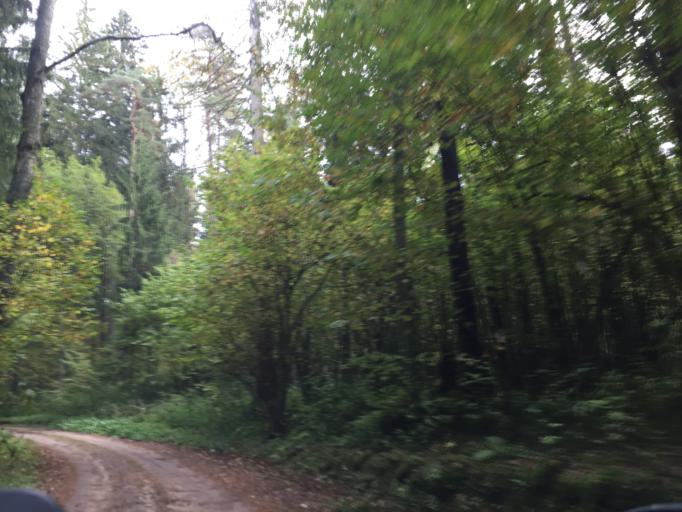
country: LV
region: Auces Novads
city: Auce
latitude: 56.5487
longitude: 23.0378
